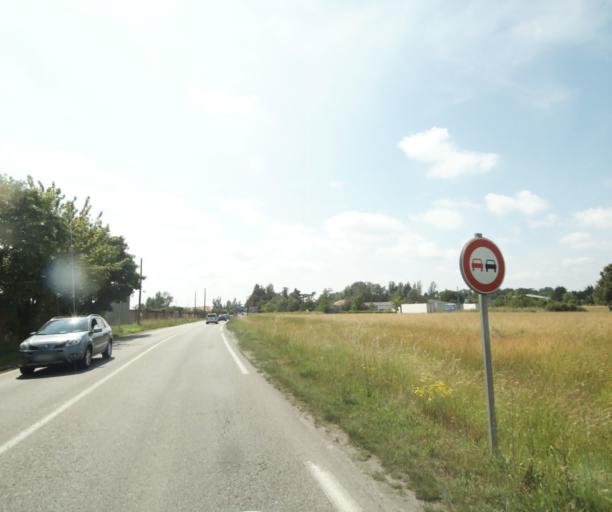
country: FR
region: Midi-Pyrenees
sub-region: Departement du Tarn-et-Garonne
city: Montauban
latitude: 44.0320
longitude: 1.3849
